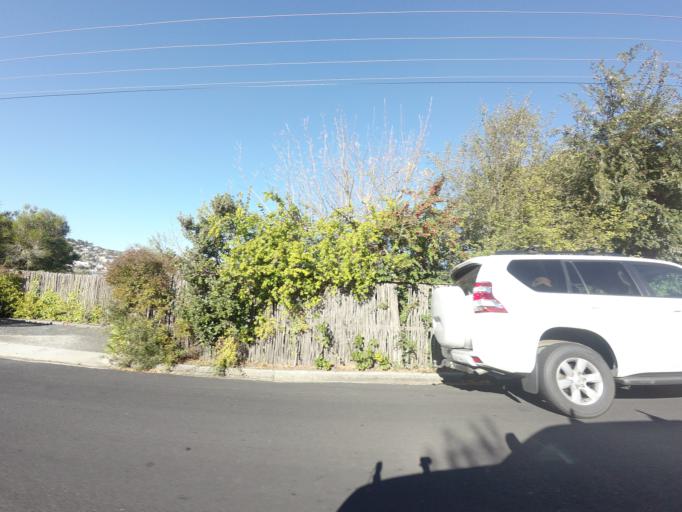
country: AU
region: Tasmania
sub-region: Clarence
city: Bellerive
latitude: -42.8720
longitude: 147.3609
